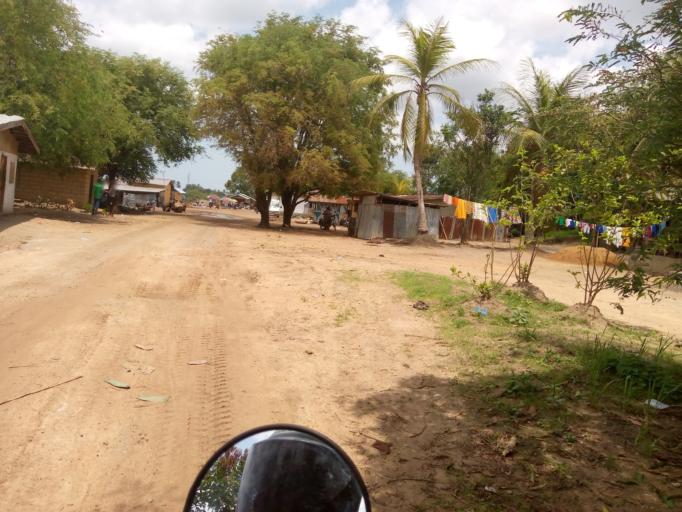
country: SL
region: Western Area
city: Waterloo
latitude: 8.3712
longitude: -12.9597
